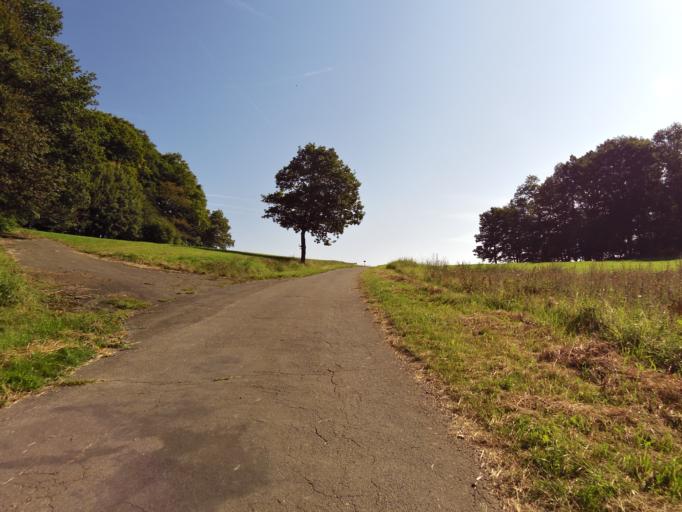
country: DE
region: Hesse
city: Lutzelbach
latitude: 49.7133
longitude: 8.7695
